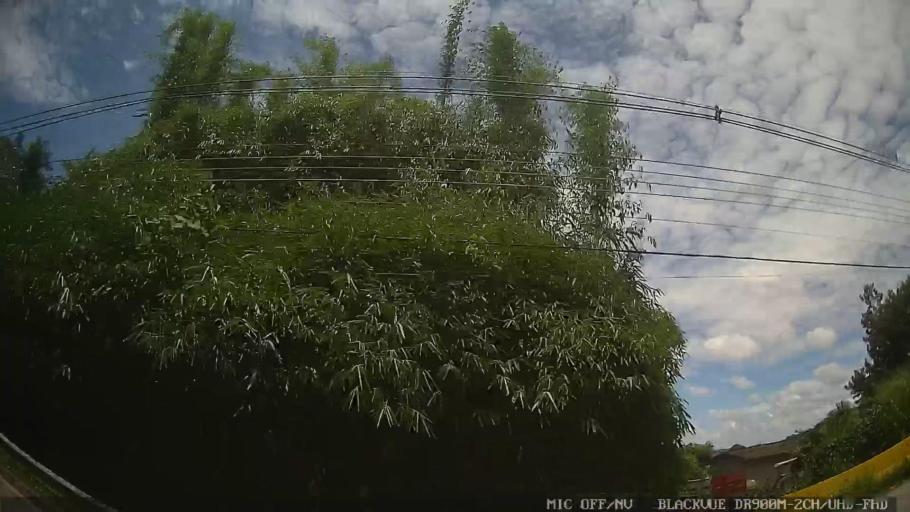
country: BR
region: Sao Paulo
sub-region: Biritiba-Mirim
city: Biritiba Mirim
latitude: -23.5574
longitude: -45.9896
